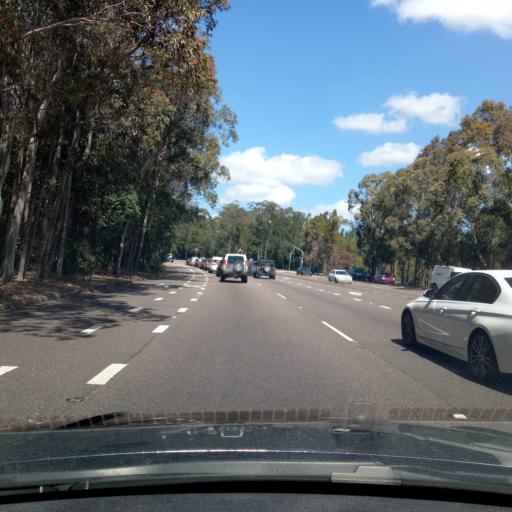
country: AU
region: New South Wales
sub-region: Wyong Shire
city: Berkeley Vale
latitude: -33.3405
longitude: 151.4286
